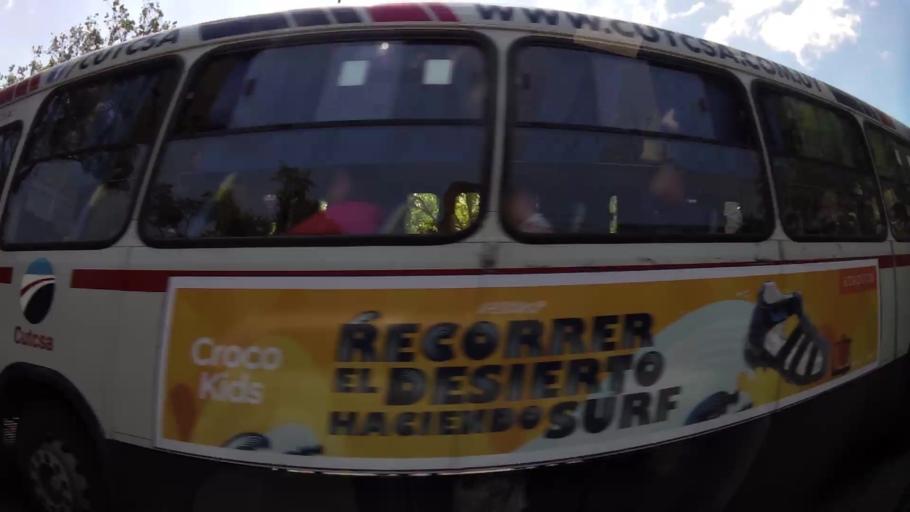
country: UY
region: Montevideo
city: Montevideo
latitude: -34.8648
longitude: -56.1966
